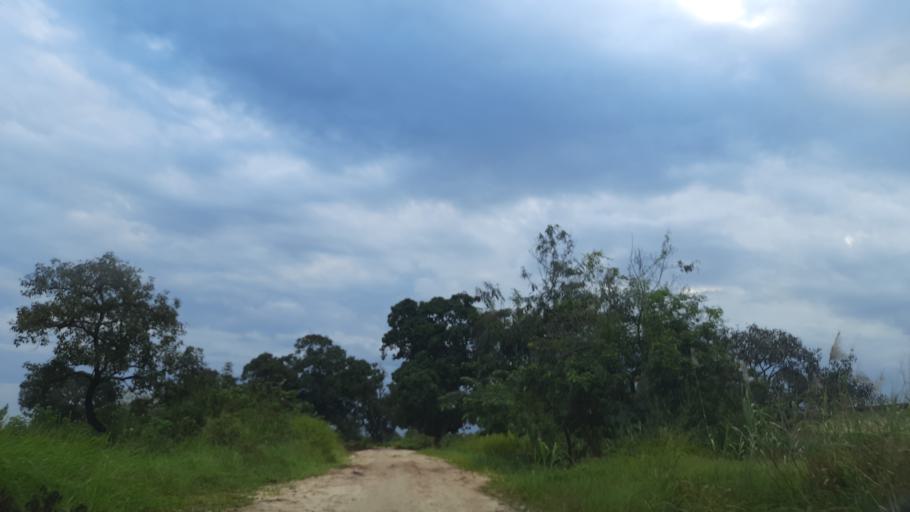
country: TZ
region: Pwani
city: Bagamoyo
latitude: -6.5245
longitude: 38.9233
